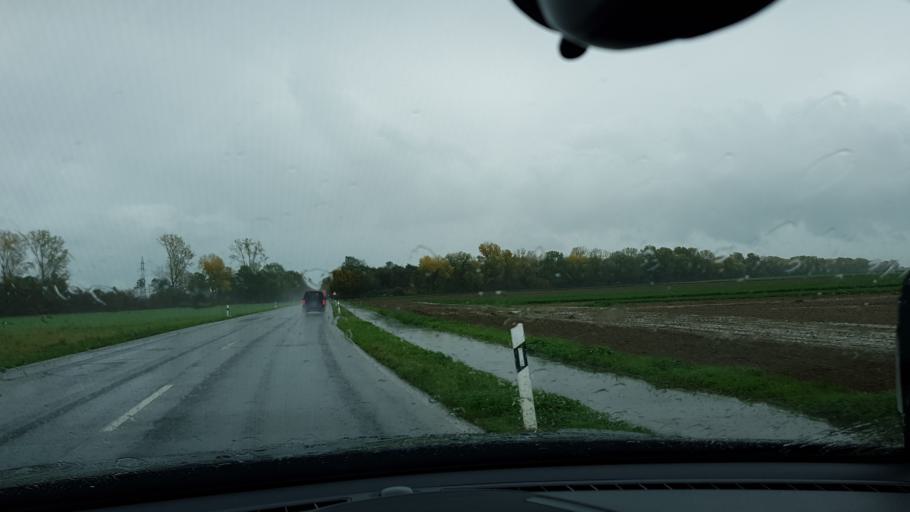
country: DE
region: North Rhine-Westphalia
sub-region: Regierungsbezirk Dusseldorf
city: Rommerskirchen
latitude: 51.0673
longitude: 6.7029
